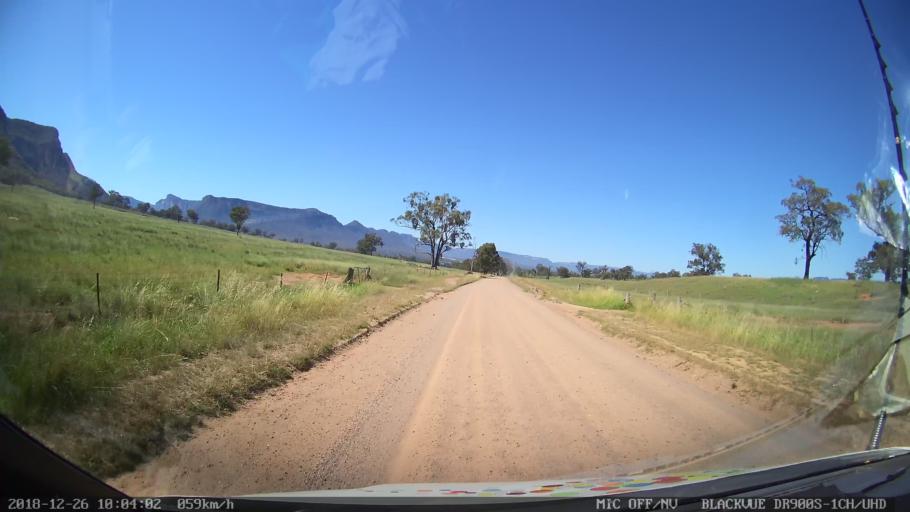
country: AU
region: New South Wales
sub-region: Mid-Western Regional
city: Kandos
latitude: -33.0667
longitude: 150.2160
